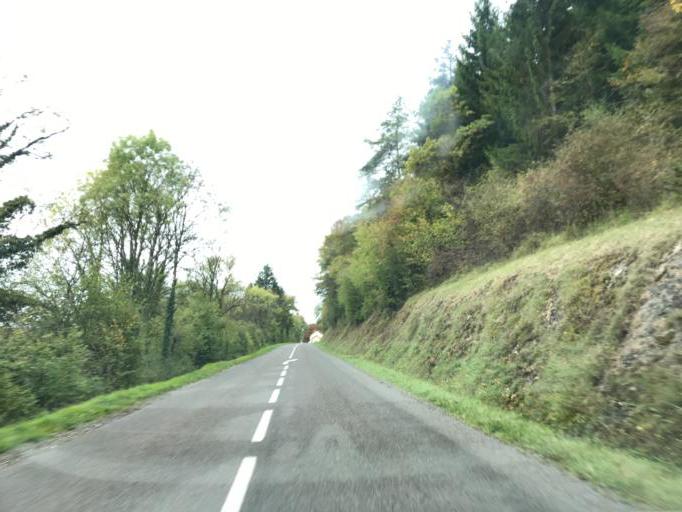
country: FR
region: Rhone-Alpes
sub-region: Departement de l'Ain
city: Cuisiat
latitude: 46.3334
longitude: 5.4370
